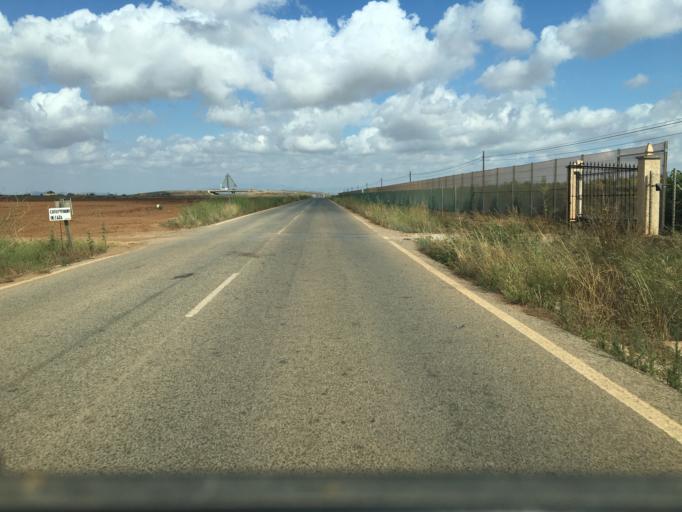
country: ES
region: Murcia
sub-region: Murcia
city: La Union
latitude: 37.6482
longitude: -0.8776
